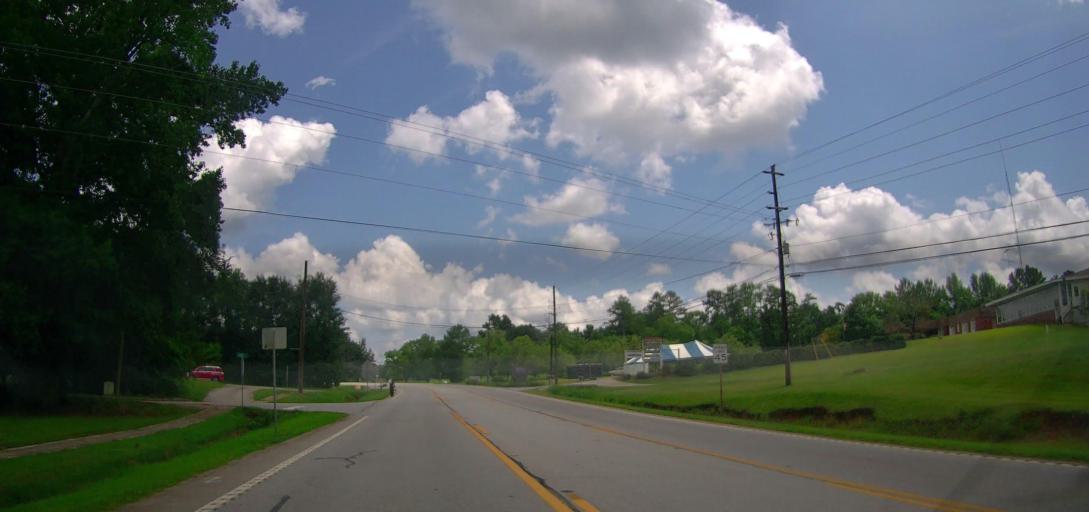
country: US
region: Georgia
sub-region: Heard County
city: Franklin
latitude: 33.2728
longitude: -85.0930
